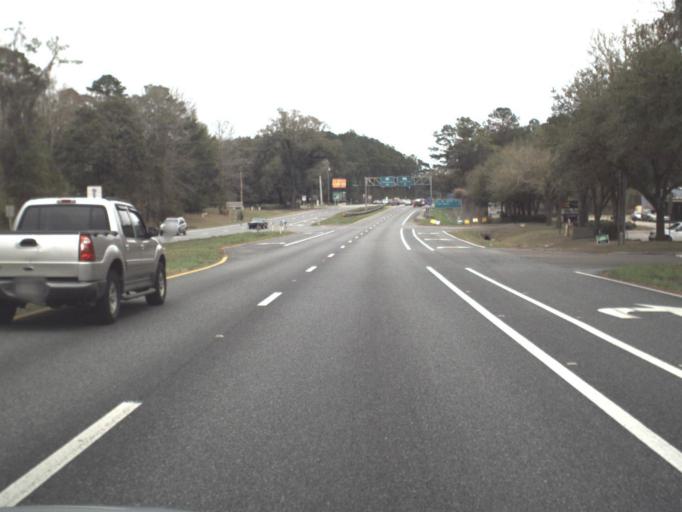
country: US
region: Florida
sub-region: Gadsden County
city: Midway
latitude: 30.5343
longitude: -84.3642
